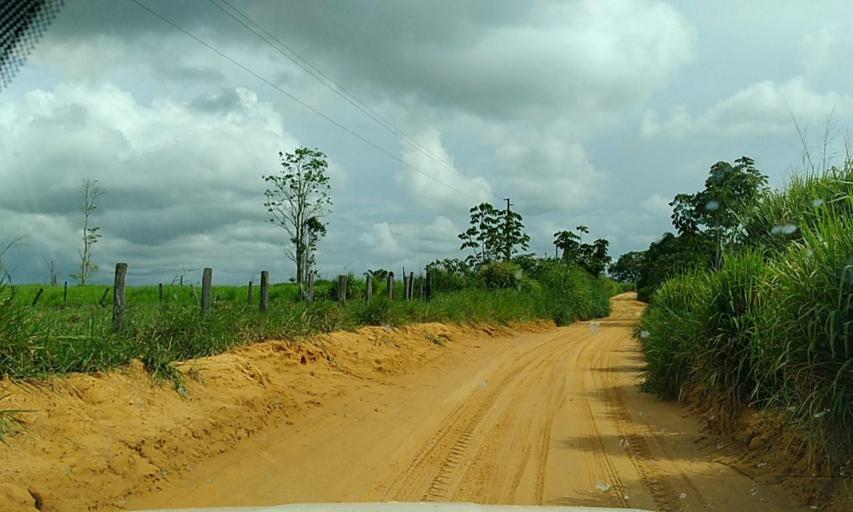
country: BR
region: Para
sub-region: Altamira
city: Altamira
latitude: -3.2341
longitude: -52.6952
